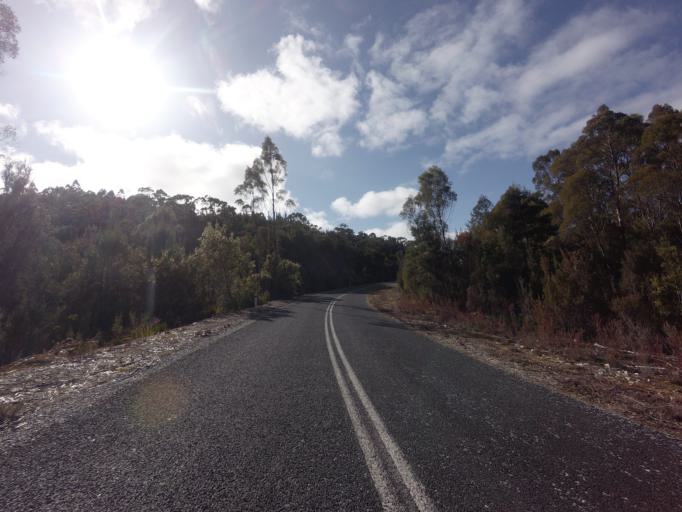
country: AU
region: Tasmania
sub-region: Huon Valley
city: Geeveston
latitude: -42.8204
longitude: 146.1111
